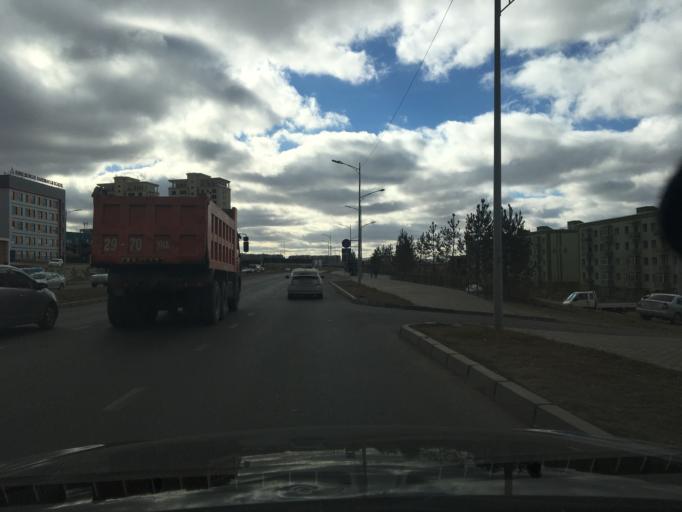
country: MN
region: Ulaanbaatar
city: Ulaanbaatar
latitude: 47.8776
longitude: 106.8512
